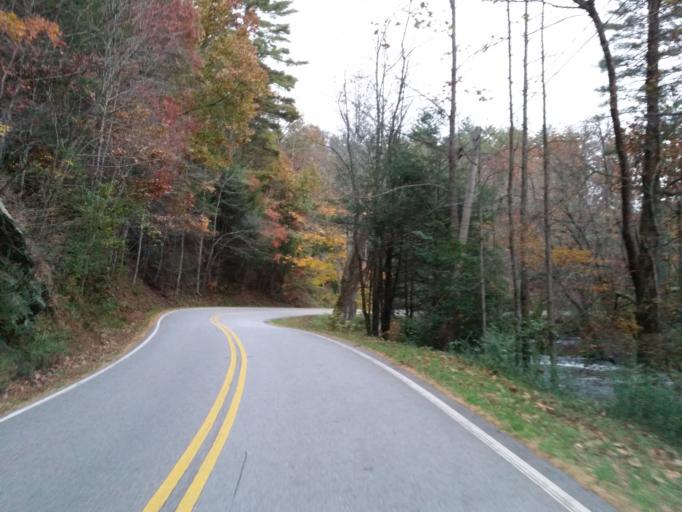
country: US
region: Georgia
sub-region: Union County
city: Blairsville
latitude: 34.7383
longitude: -84.0817
